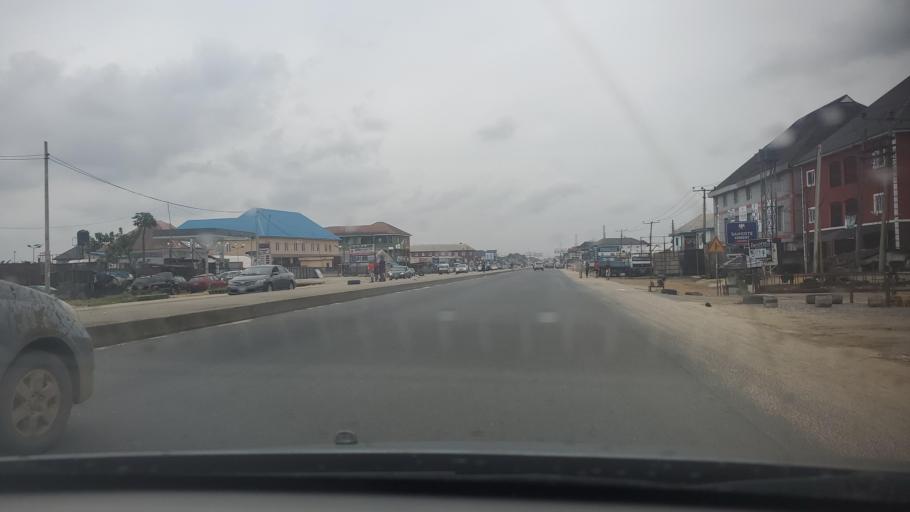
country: NG
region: Rivers
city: Port Harcourt
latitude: 4.8695
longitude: 6.9783
